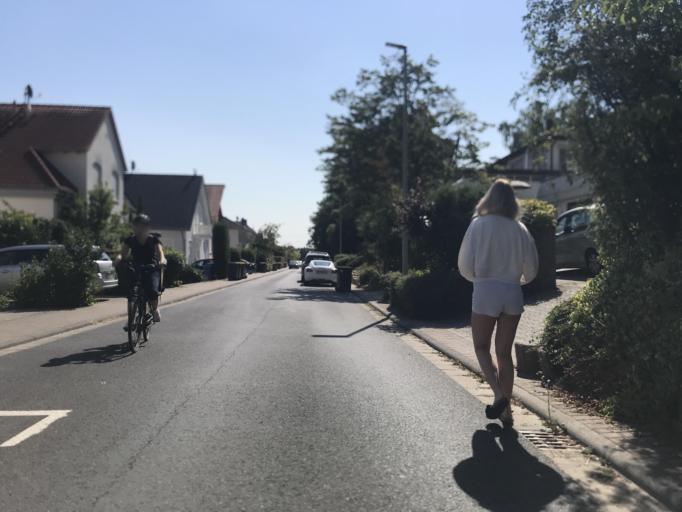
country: DE
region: Hesse
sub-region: Regierungsbezirk Darmstadt
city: Eltville
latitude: 50.0419
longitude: 8.1073
